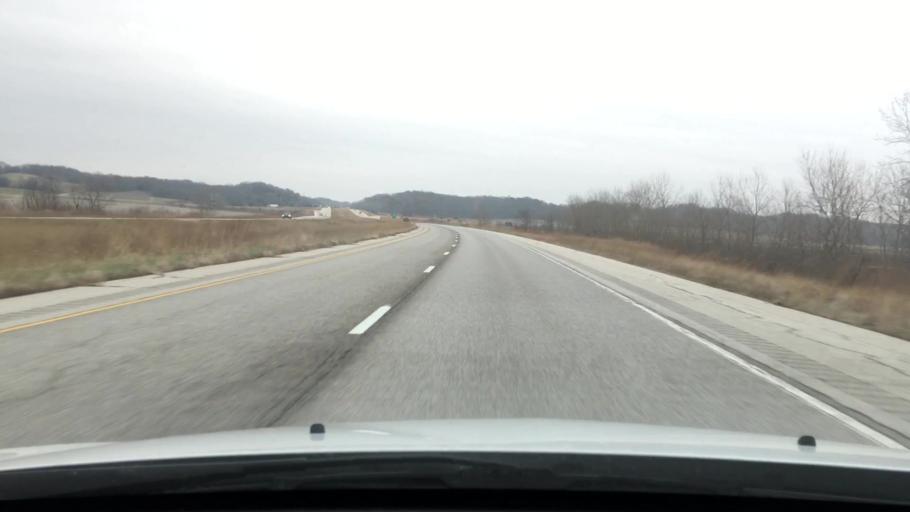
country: US
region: Illinois
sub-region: Pike County
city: Griggsville
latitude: 39.6852
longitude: -90.5865
